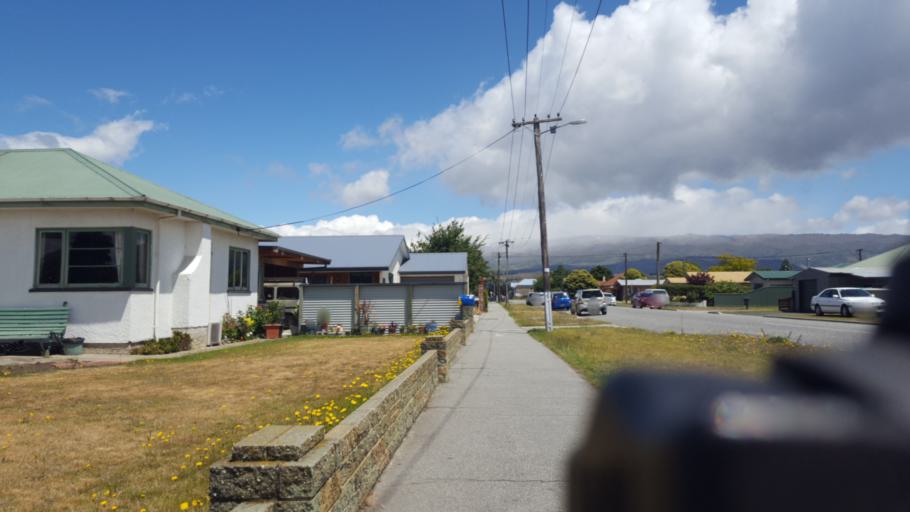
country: NZ
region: Otago
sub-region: Queenstown-Lakes District
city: Wanaka
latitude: -45.2485
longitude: 169.3888
